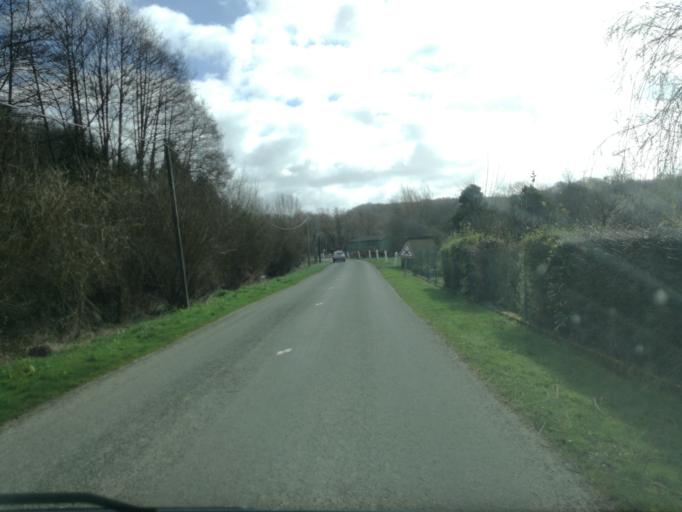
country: FR
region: Haute-Normandie
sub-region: Departement de la Seine-Maritime
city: Bretteville-du-Grand-Caux
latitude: 49.7072
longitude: 0.4315
